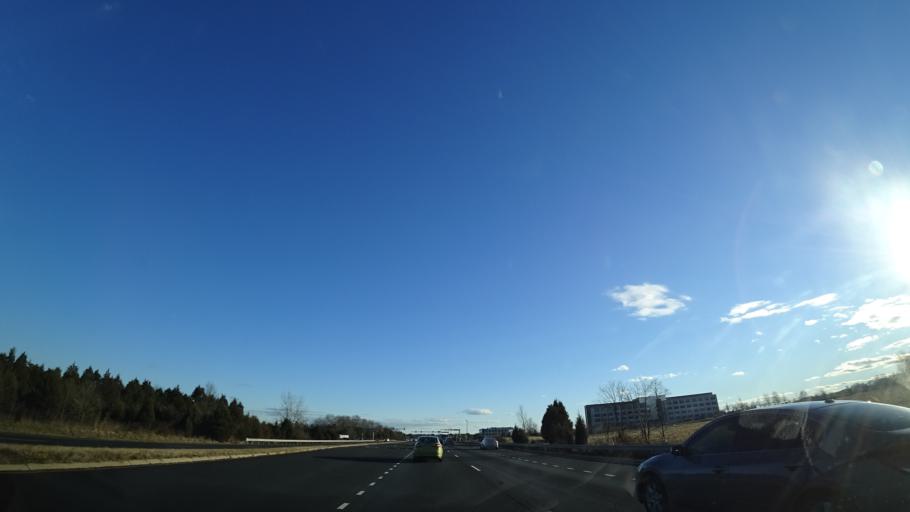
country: US
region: Virginia
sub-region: Prince William County
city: Bull Run
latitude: 38.7564
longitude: -77.5292
